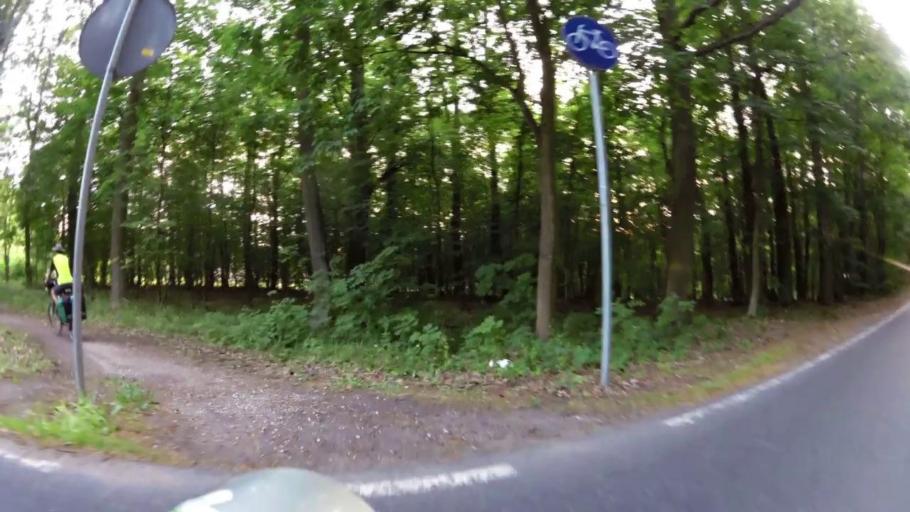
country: PL
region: Kujawsko-Pomorskie
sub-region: Powiat bydgoski
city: Dabrowa Chelminska
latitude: 53.1760
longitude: 18.2764
